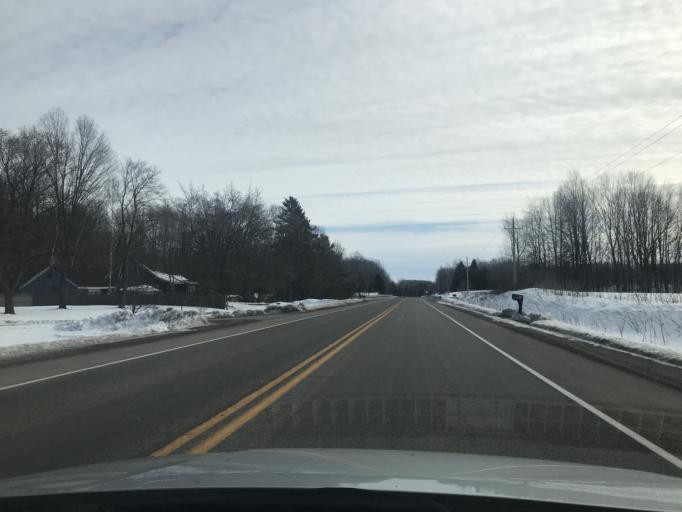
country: US
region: Wisconsin
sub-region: Oconto County
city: Oconto Falls
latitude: 44.8916
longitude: -88.1693
